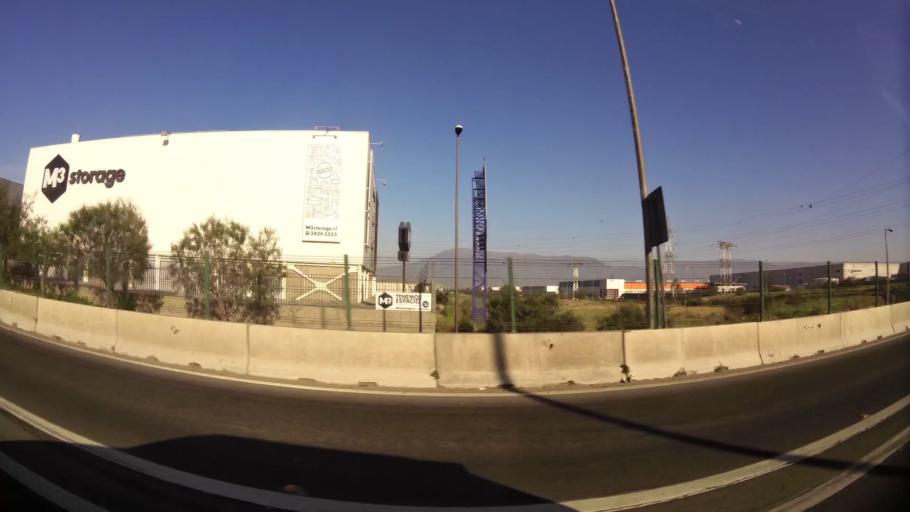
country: CL
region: Santiago Metropolitan
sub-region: Provincia de Santiago
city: Lo Prado
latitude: -33.4332
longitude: -70.7853
